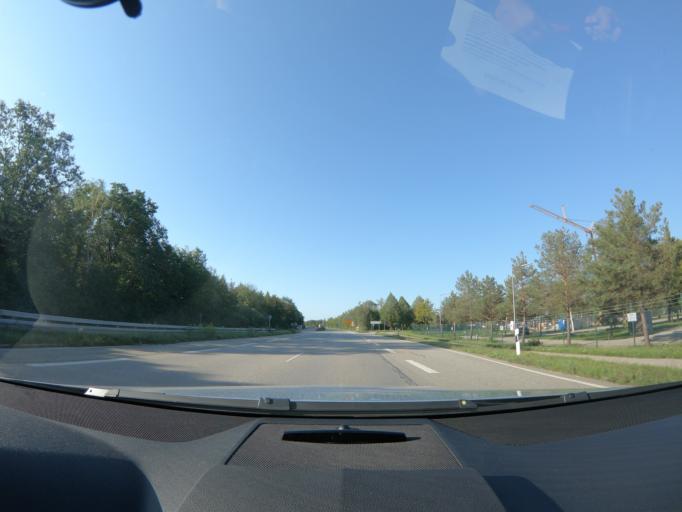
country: DE
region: Bavaria
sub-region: Upper Bavaria
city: Oberschleissheim
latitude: 48.2441
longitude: 11.6018
